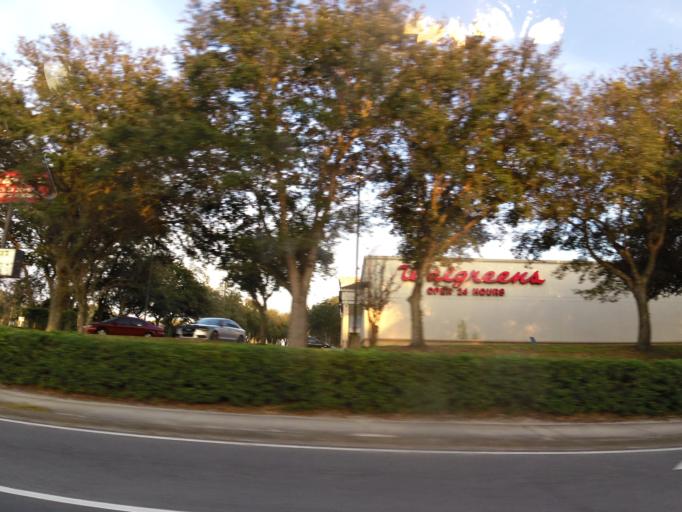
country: US
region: Florida
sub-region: Volusia County
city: North DeLand
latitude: 29.0543
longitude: -81.3042
